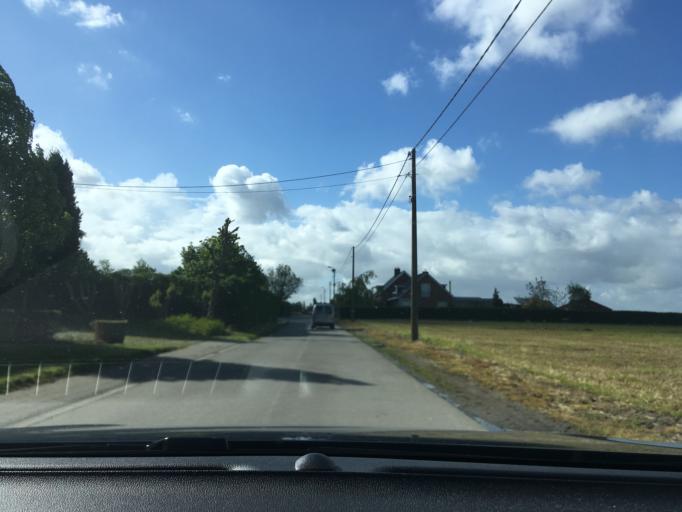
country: BE
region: Flanders
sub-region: Provincie West-Vlaanderen
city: Hooglede
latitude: 51.0004
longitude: 3.0757
